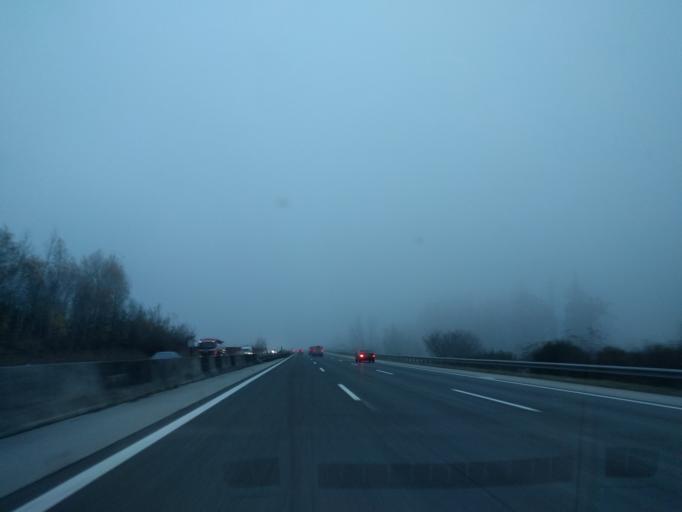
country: AT
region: Lower Austria
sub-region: Politischer Bezirk Amstetten
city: Strengberg
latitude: 48.1243
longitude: 14.6133
